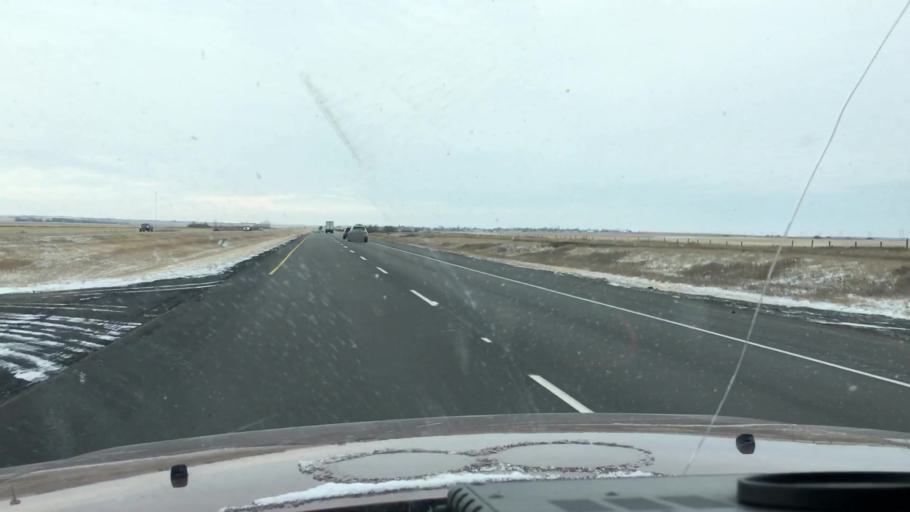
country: CA
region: Saskatchewan
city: Saskatoon
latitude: 51.8382
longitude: -106.5039
